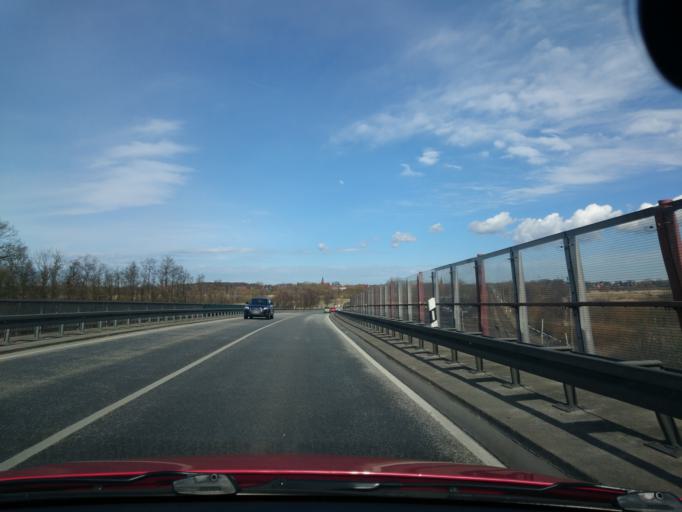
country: DE
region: Mecklenburg-Vorpommern
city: Ribnitz-Damgarten
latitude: 54.2428
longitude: 12.4593
